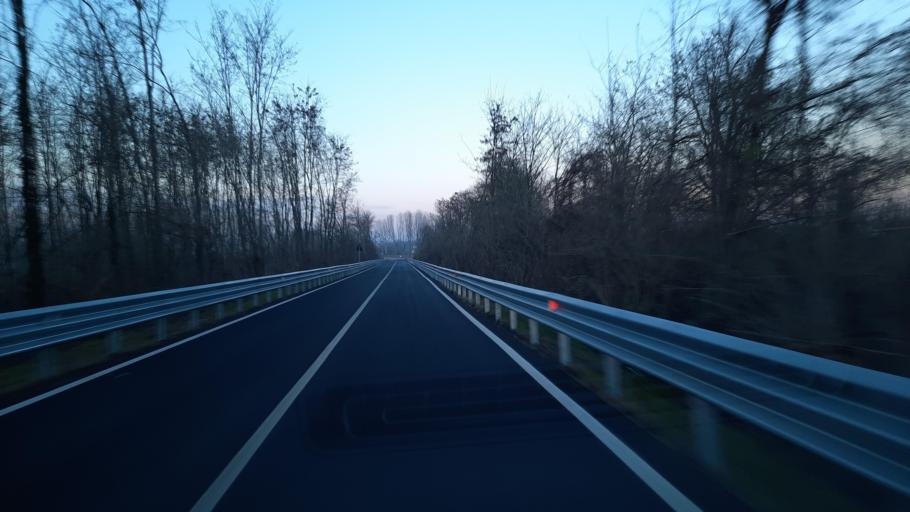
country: IT
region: Piedmont
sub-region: Provincia di Vercelli
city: Trino
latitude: 45.1769
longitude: 8.2942
